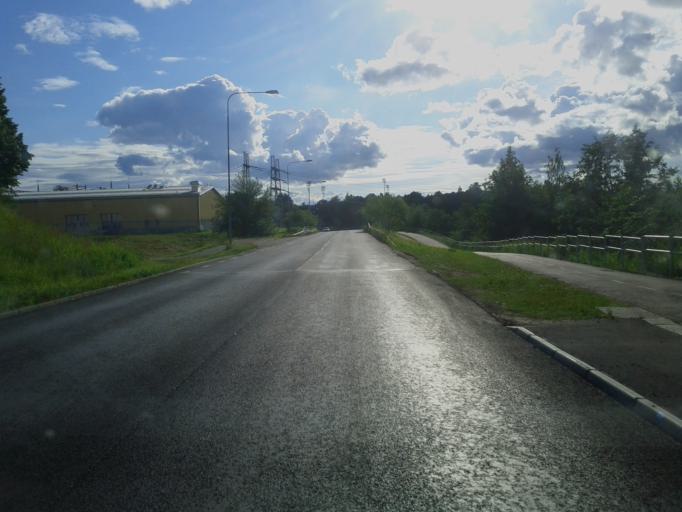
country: SE
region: Dalarna
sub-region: Borlange Kommun
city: Borlaenge
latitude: 60.4962
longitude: 15.4493
